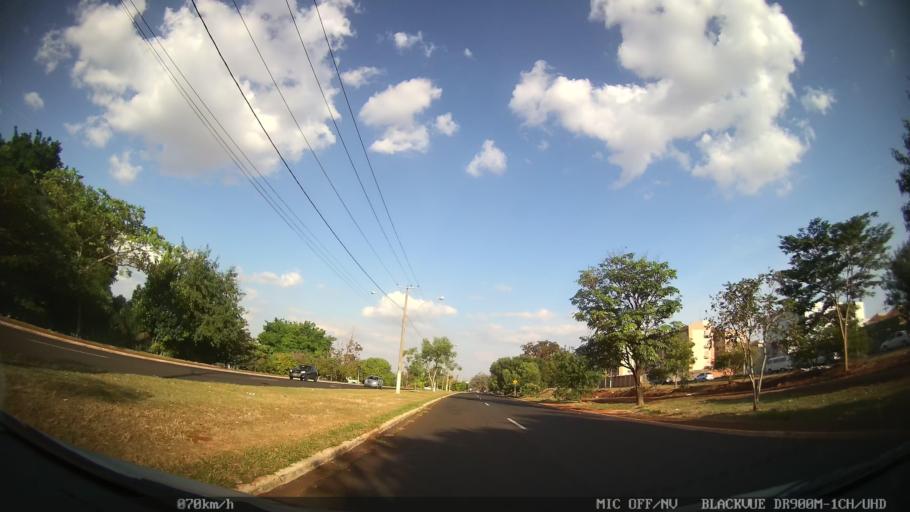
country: BR
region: Sao Paulo
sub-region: Ribeirao Preto
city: Ribeirao Preto
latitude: -21.1374
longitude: -47.8357
